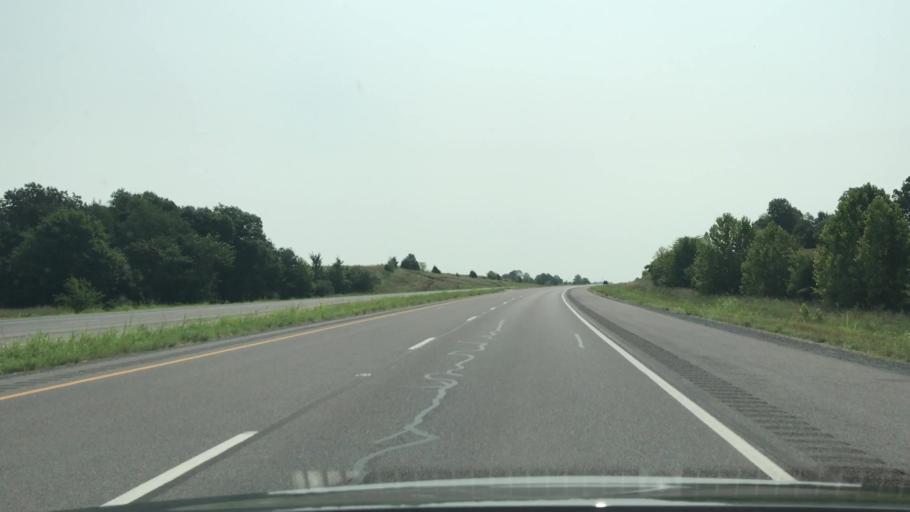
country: US
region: Kentucky
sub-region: Graves County
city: Mayfield
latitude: 36.6910
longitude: -88.5535
